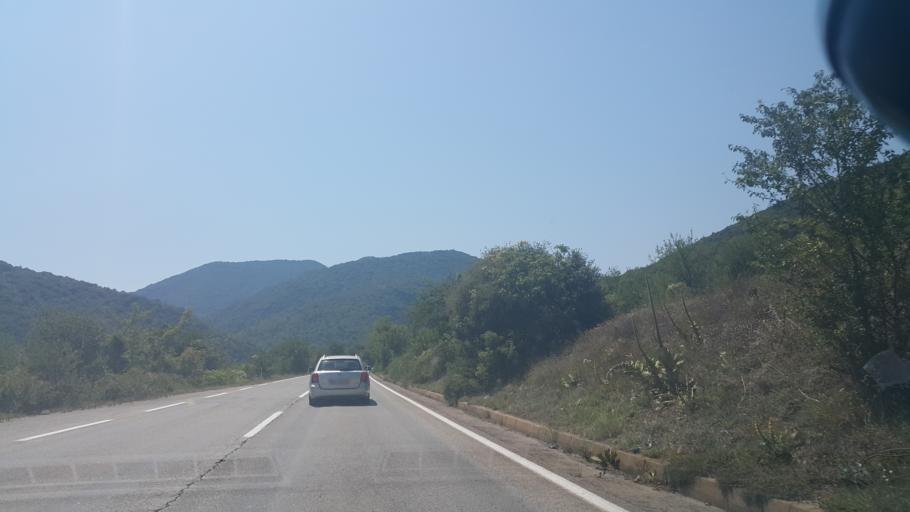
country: MK
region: Gevgelija
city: Miravci
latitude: 41.3784
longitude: 22.3954
